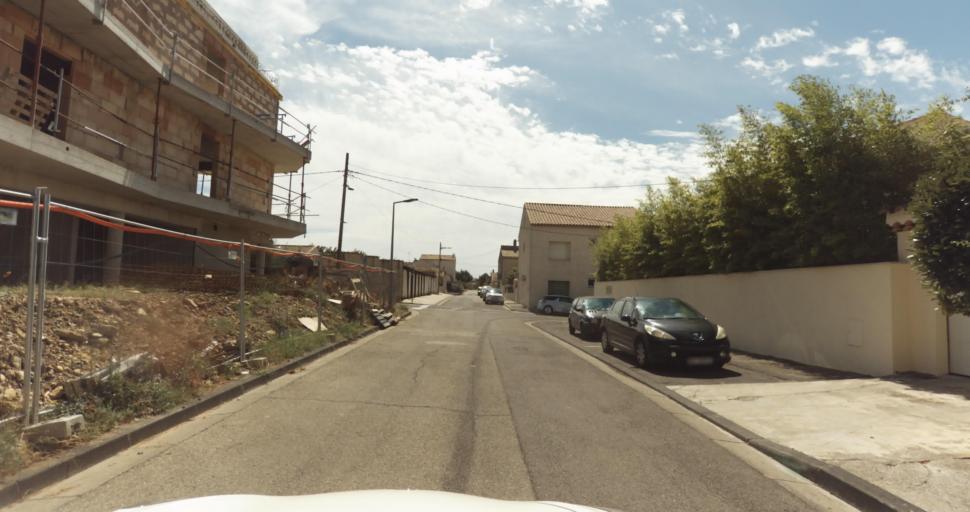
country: FR
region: Provence-Alpes-Cote d'Azur
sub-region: Departement des Bouches-du-Rhone
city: Miramas
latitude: 43.5848
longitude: 5.0096
